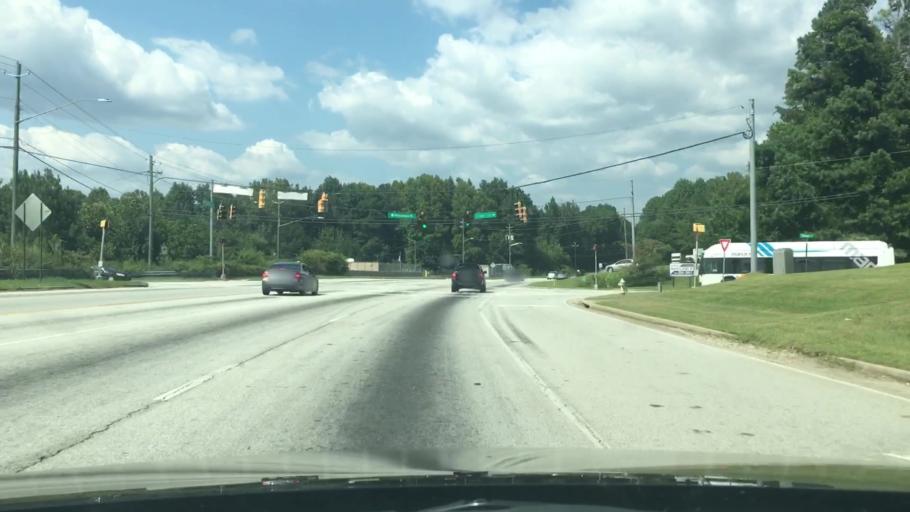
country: US
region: Georgia
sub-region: DeKalb County
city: Lithonia
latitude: 33.7065
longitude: -84.1304
